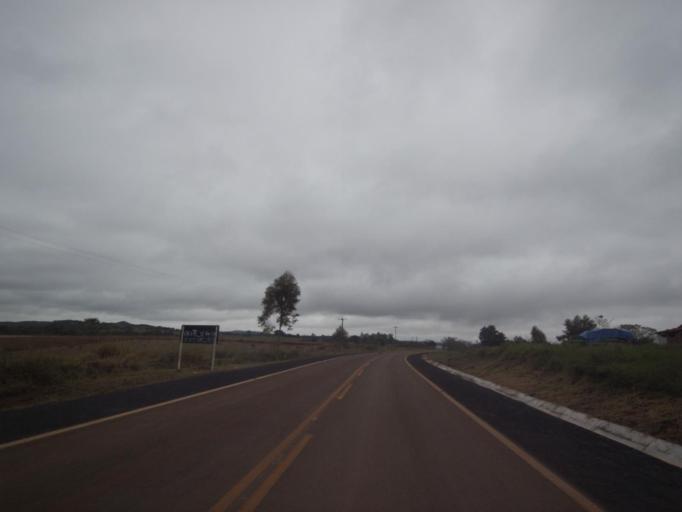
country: AR
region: Misiones
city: El Soberbio
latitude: -27.2935
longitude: -54.1739
